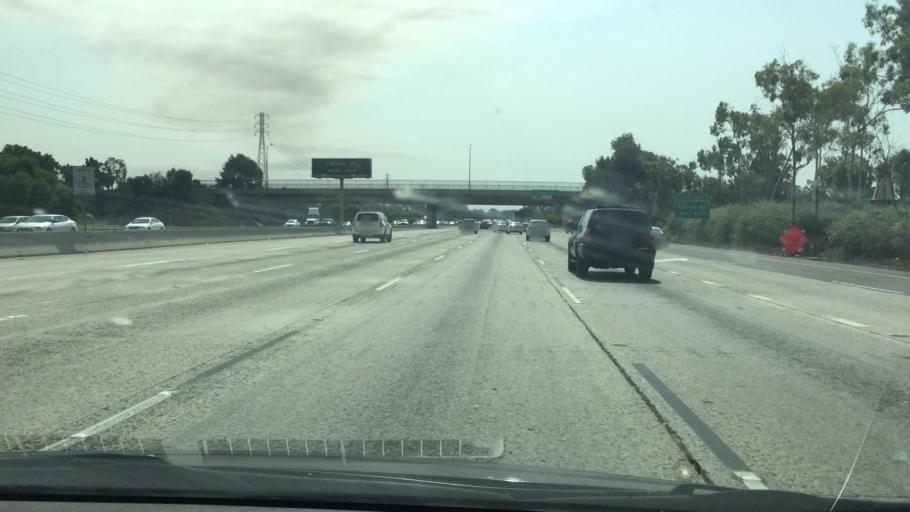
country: US
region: California
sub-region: Orange County
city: Irvine
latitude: 33.6726
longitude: -117.8338
